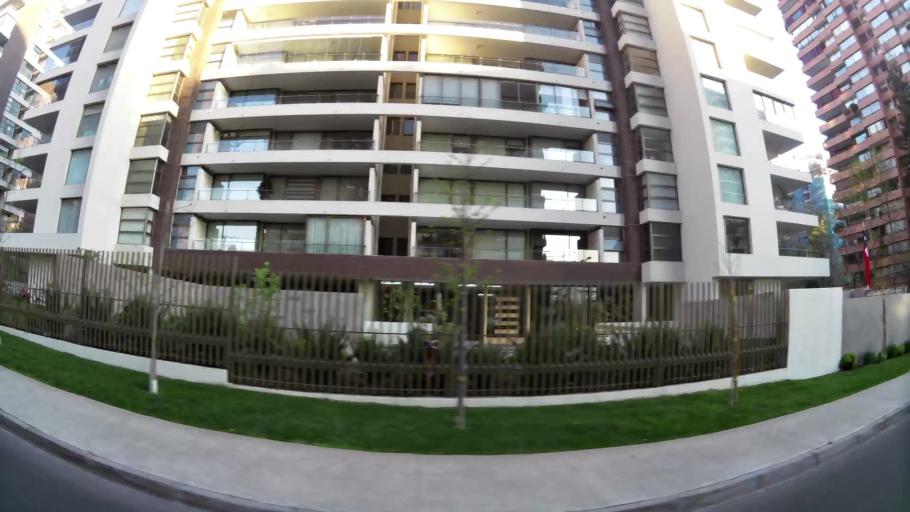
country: CL
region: Santiago Metropolitan
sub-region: Provincia de Santiago
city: Villa Presidente Frei, Nunoa, Santiago, Chile
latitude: -33.3967
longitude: -70.5646
